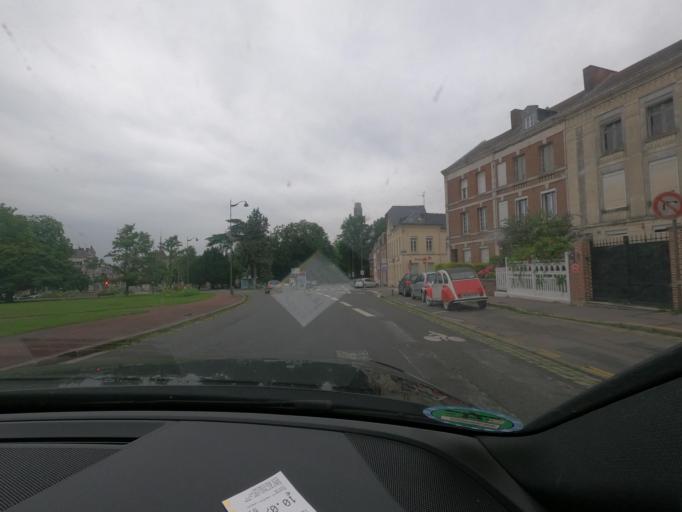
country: FR
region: Picardie
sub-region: Departement de la Somme
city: Amiens
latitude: 49.8873
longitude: 2.3036
